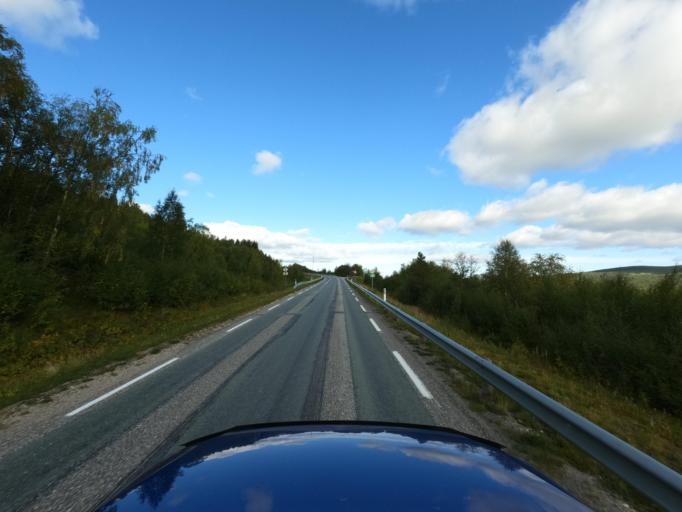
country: NO
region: Finnmark Fylke
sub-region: Karasjok
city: Karasjohka
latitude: 69.4271
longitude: 25.7940
